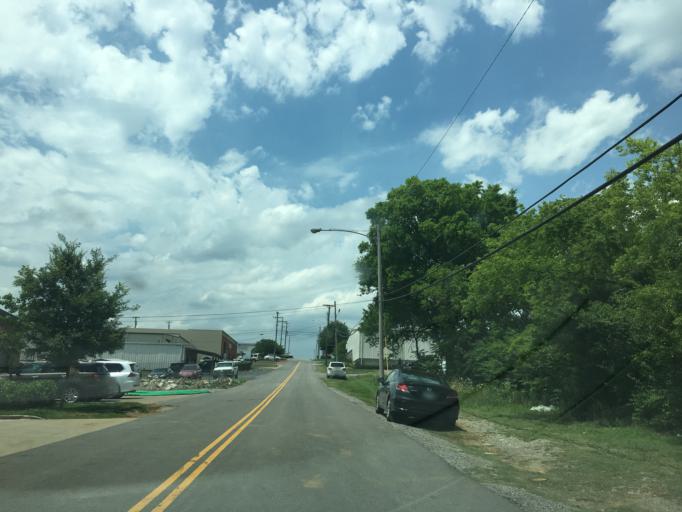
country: US
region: Tennessee
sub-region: Davidson County
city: Oak Hill
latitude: 36.1186
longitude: -86.7518
